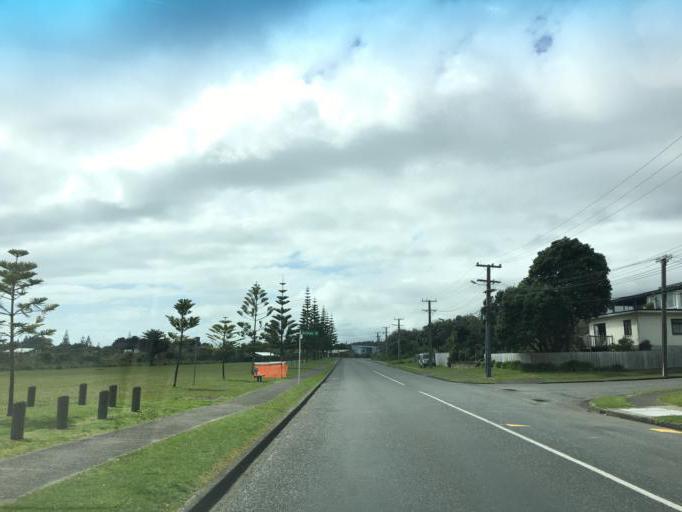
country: NZ
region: Wellington
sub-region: Kapiti Coast District
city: Paraparaumu
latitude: -40.8698
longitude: 175.0197
